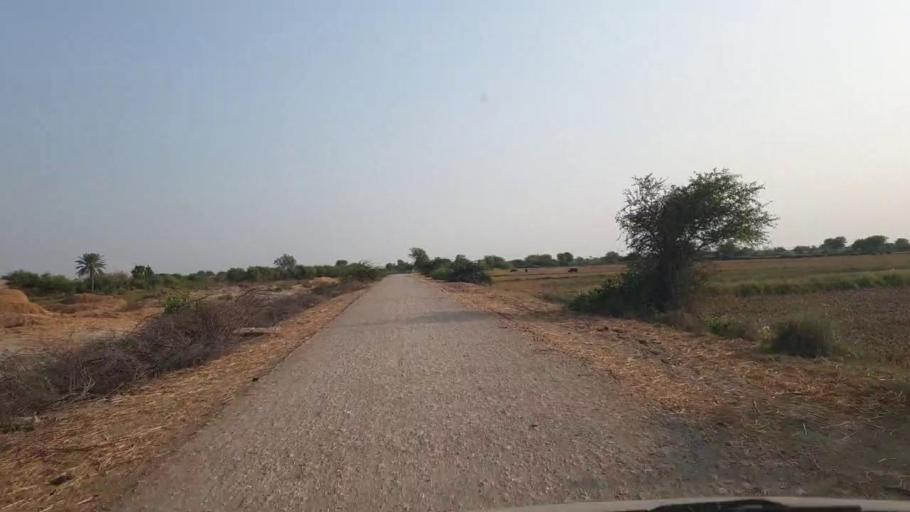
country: PK
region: Sindh
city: Rajo Khanani
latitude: 25.0155
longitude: 68.7863
